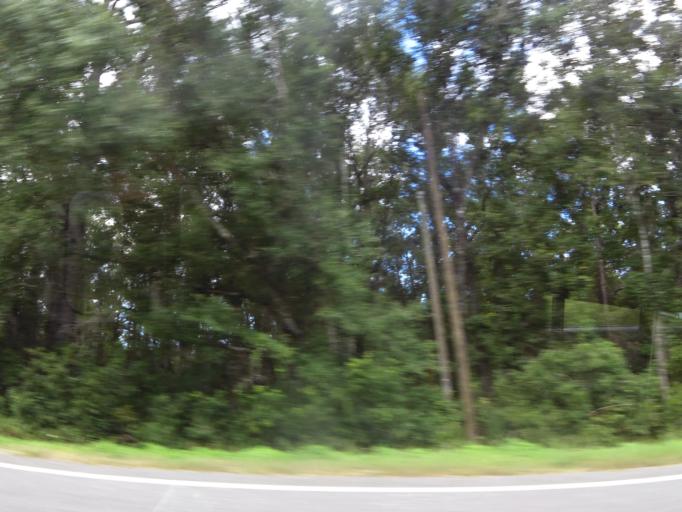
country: US
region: Florida
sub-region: Saint Johns County
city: Saint Augustine South
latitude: 29.8196
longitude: -81.4861
